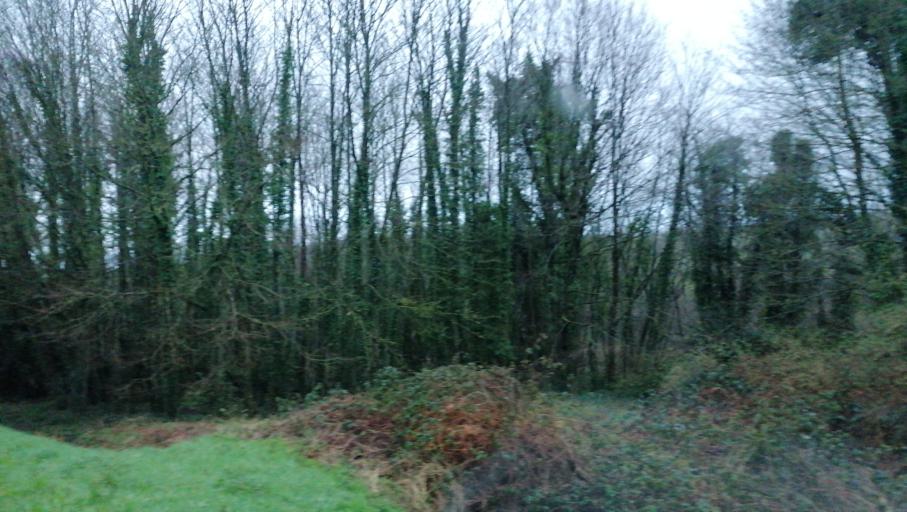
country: FR
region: Brittany
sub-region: Departement des Cotes-d'Armor
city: Lanrodec
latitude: 48.4746
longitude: -2.9846
